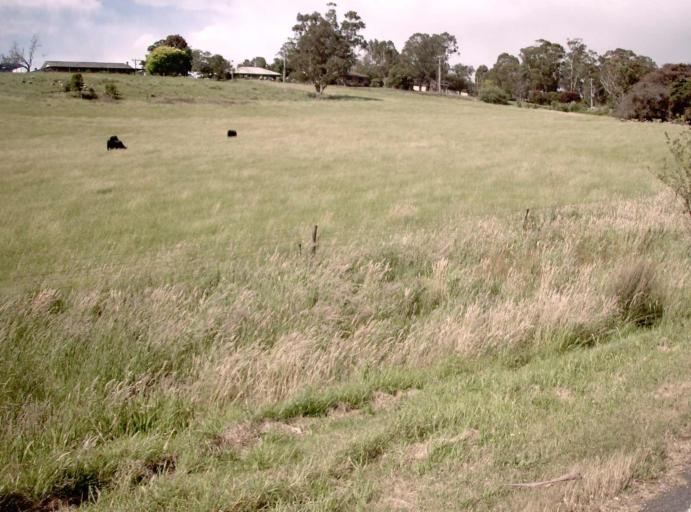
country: AU
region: Victoria
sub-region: Latrobe
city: Traralgon
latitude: -38.1490
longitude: 146.4727
